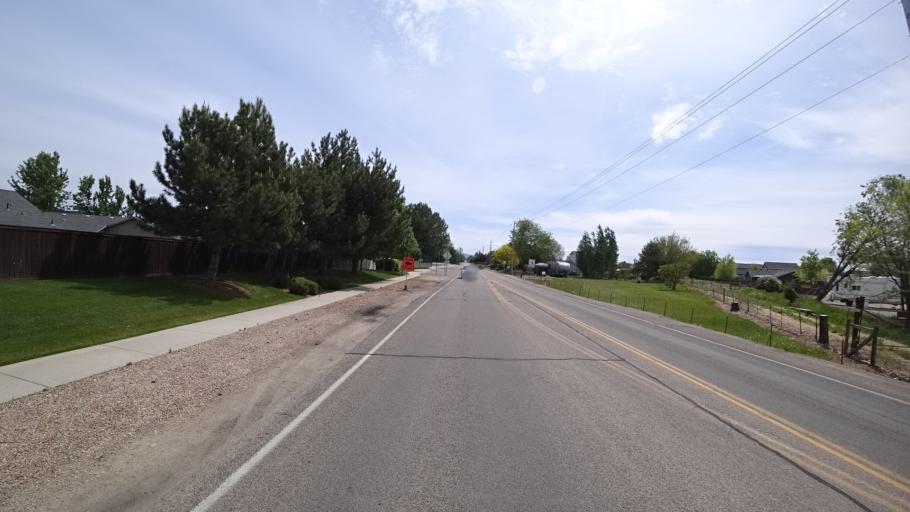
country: US
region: Idaho
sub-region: Ada County
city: Meridian
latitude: 43.5612
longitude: -116.3336
